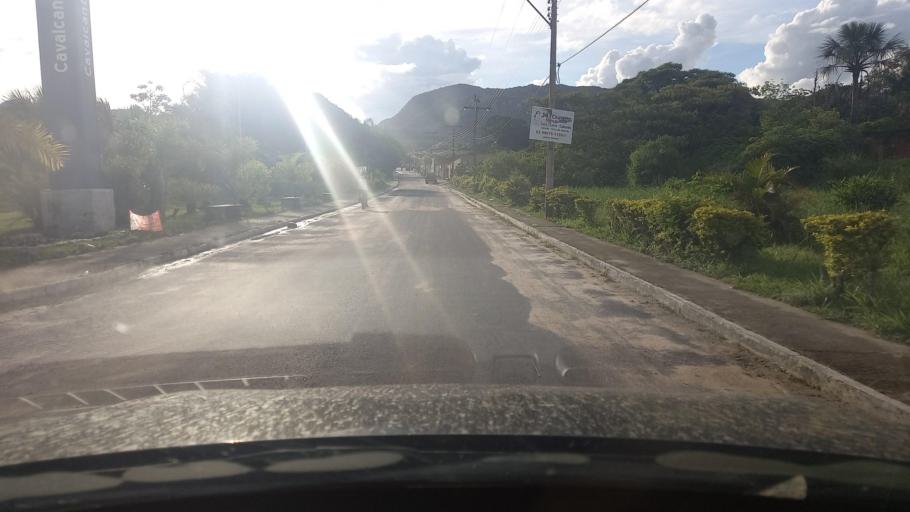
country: BR
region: Goias
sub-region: Cavalcante
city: Cavalcante
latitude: -13.7969
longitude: -47.4560
